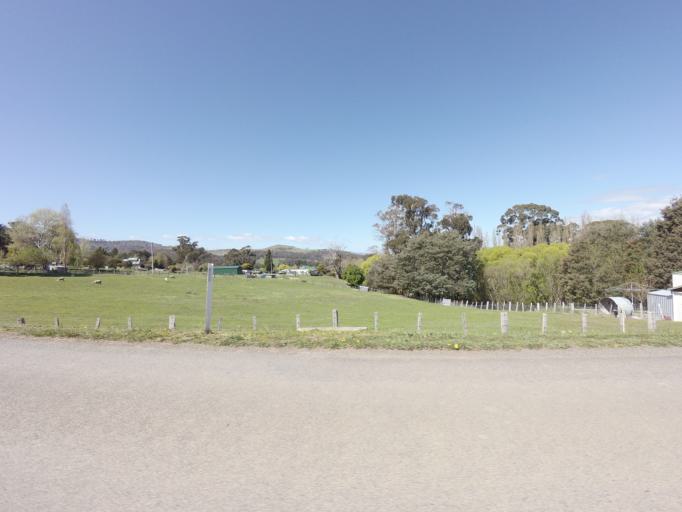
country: AU
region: Tasmania
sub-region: Derwent Valley
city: New Norfolk
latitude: -42.6705
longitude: 146.7902
